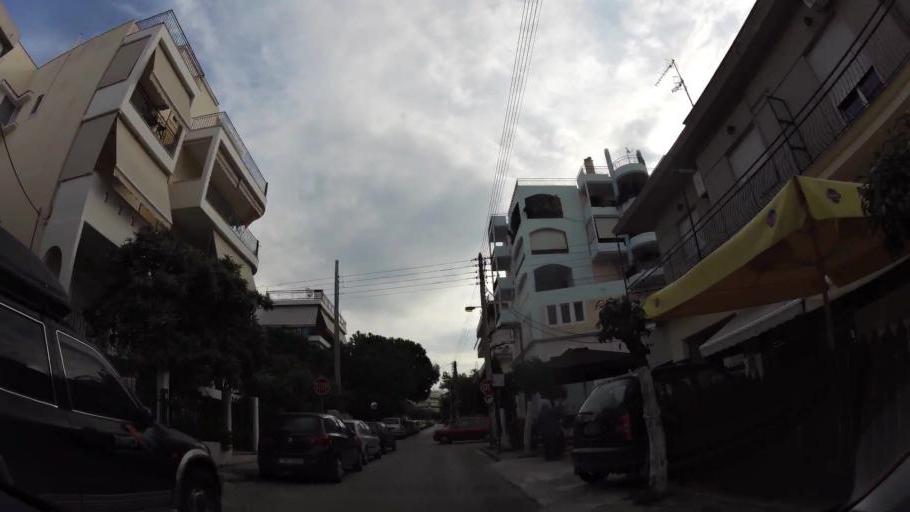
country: GR
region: Attica
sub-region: Nomarchia Athinas
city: Palaio Faliro
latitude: 37.9311
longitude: 23.7070
